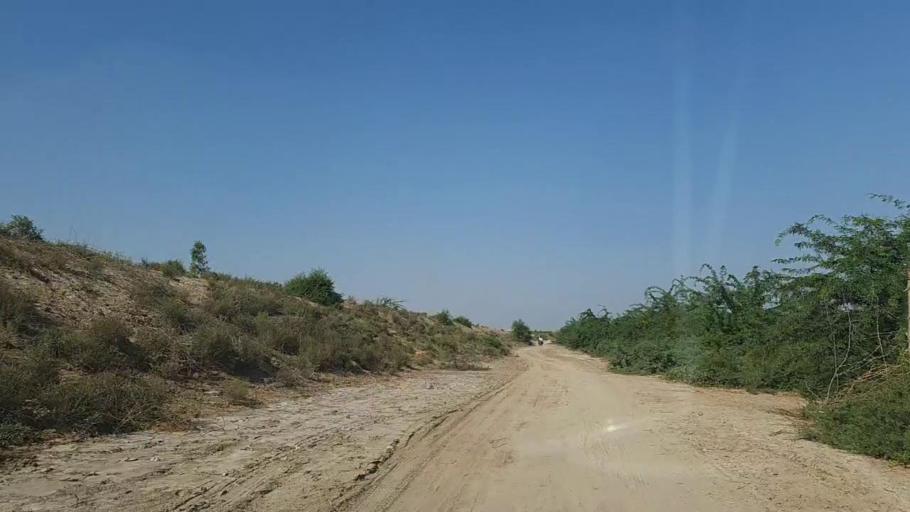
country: PK
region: Sindh
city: Chuhar Jamali
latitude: 24.5760
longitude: 68.0296
